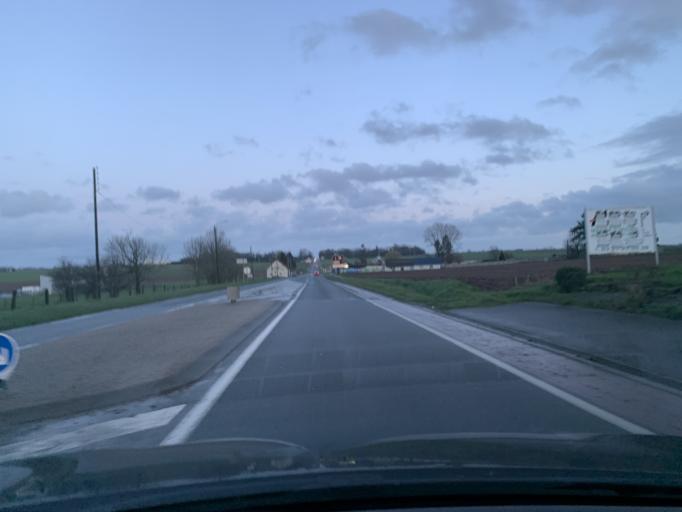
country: FR
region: Nord-Pas-de-Calais
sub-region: Departement du Nord
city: Rieux-en-Cambresis
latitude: 50.1538
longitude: 3.3256
